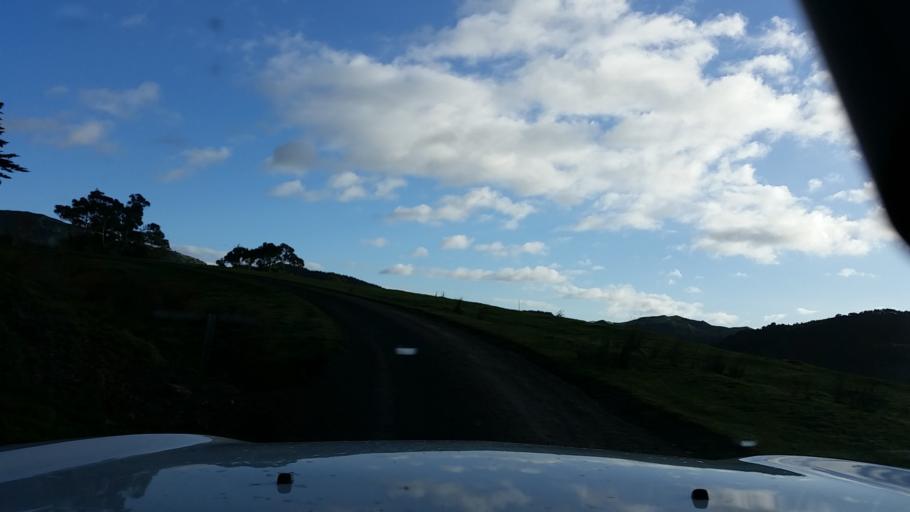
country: NZ
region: Wellington
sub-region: South Wairarapa District
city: Waipawa
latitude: -41.2645
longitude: 175.6855
